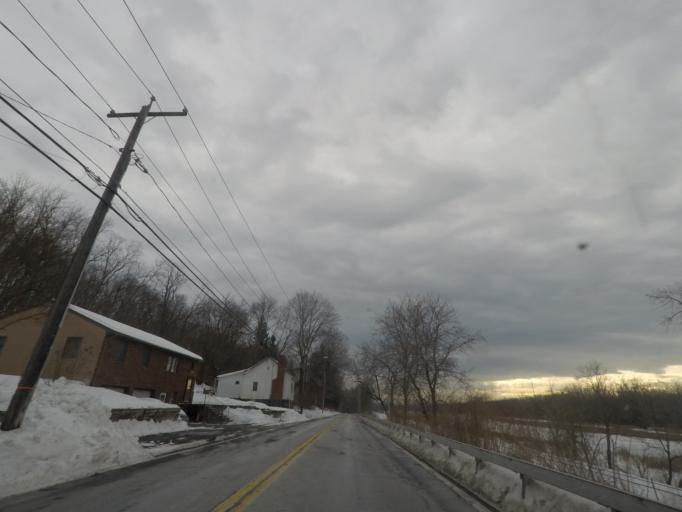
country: US
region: New York
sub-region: Rensselaer County
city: Castleton-on-Hudson
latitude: 42.4922
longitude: -73.7683
